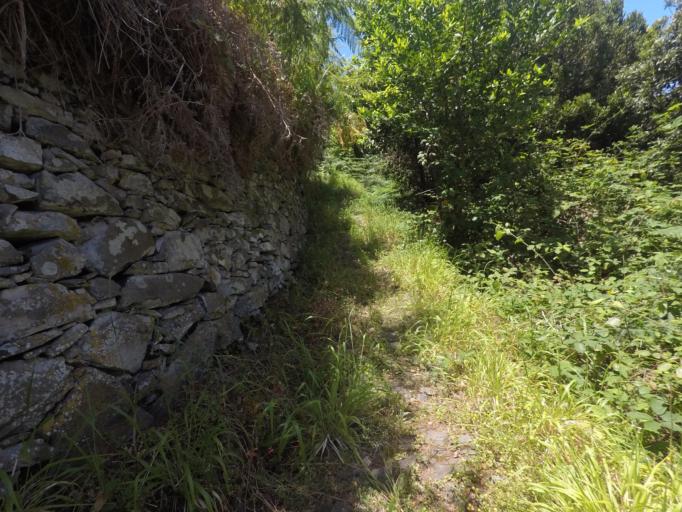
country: PT
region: Madeira
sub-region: Porto Moniz
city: Porto Moniz
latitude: 32.8311
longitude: -17.1342
